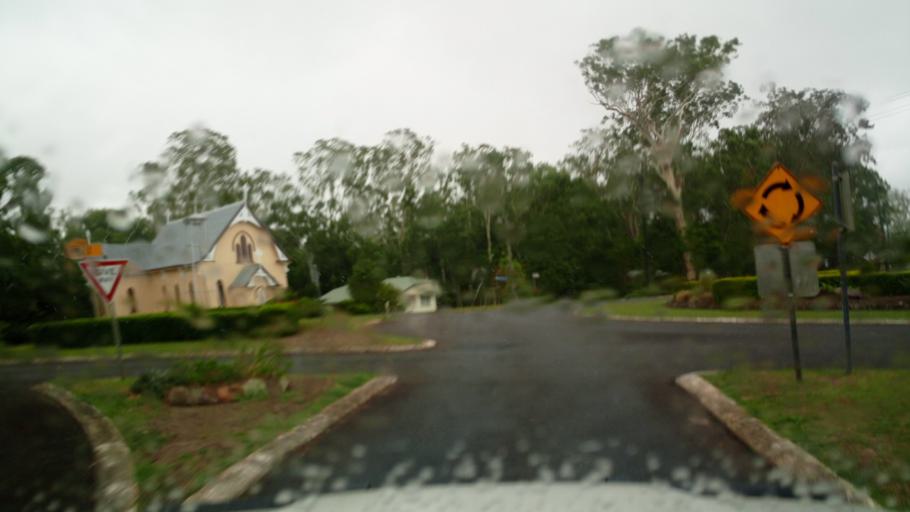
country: AU
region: Queensland
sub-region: Tablelands
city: Tolga
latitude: -17.2688
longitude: 145.5812
